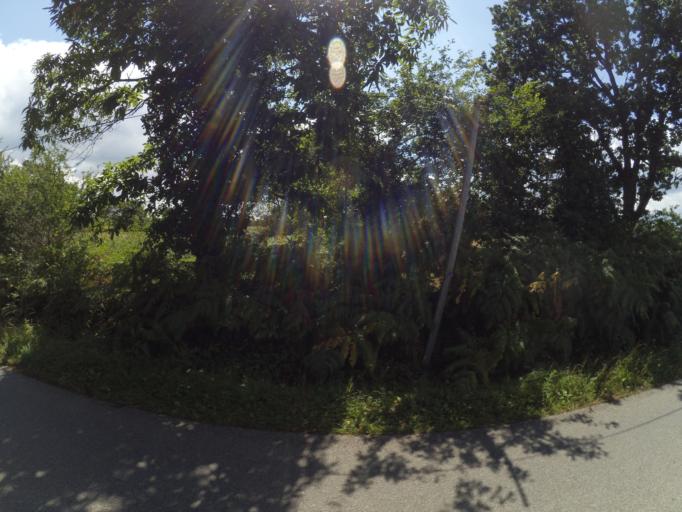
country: FR
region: Brittany
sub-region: Departement du Morbihan
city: Landaul
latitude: 47.7354
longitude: -3.0490
